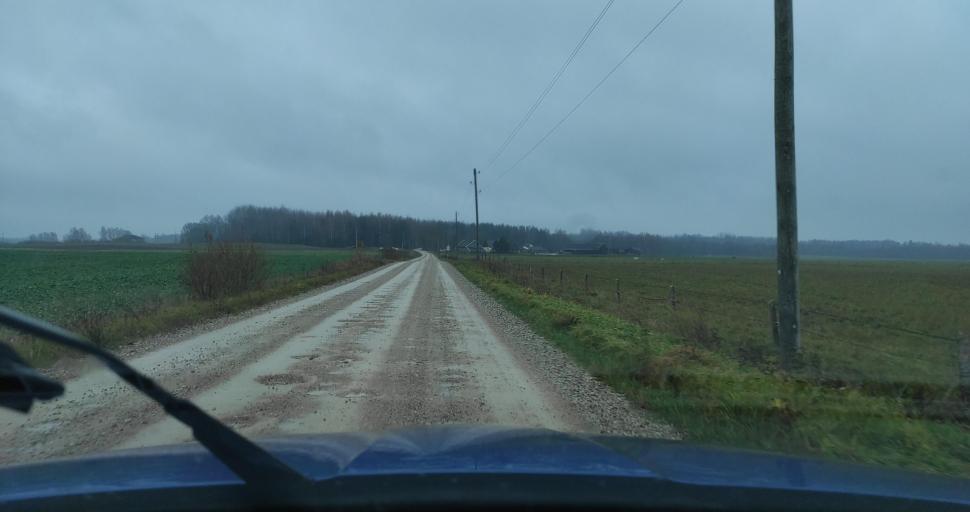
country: LV
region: Alsunga
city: Alsunga
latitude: 56.9023
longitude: 21.6259
